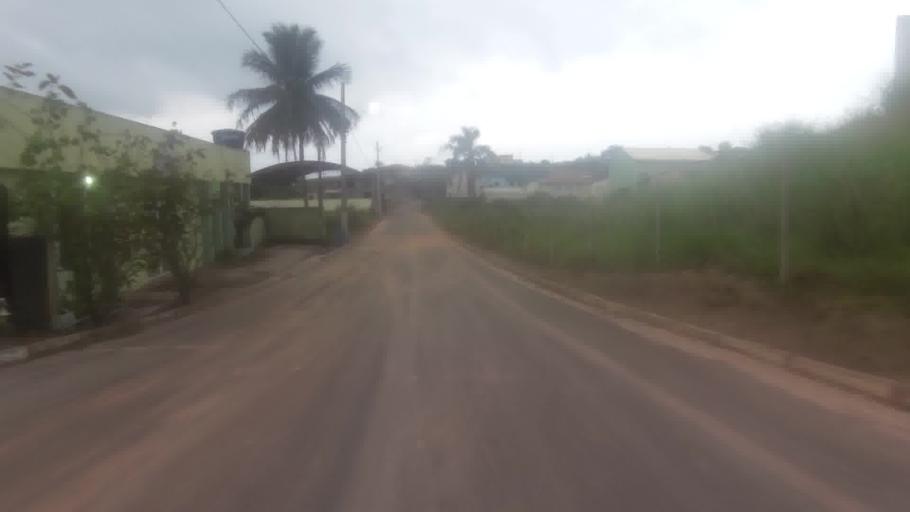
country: BR
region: Espirito Santo
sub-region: Piuma
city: Piuma
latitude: -20.8014
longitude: -40.5961
